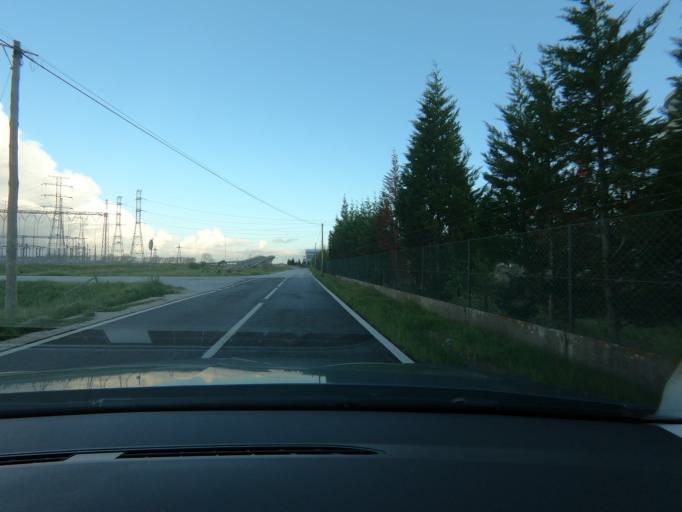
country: PT
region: Lisbon
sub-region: Alenquer
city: Carregado
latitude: 39.0136
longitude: -8.9529
